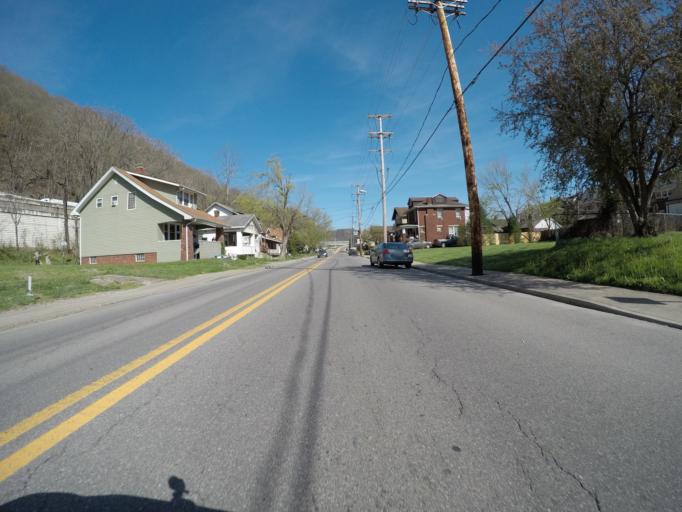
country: US
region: West Virginia
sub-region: Kanawha County
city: Charleston
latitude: 38.3354
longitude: -81.6017
